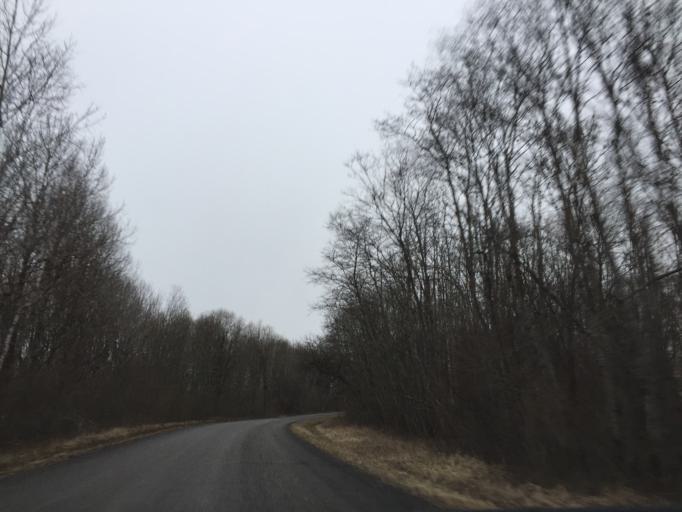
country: EE
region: Laeaene
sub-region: Lihula vald
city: Lihula
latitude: 58.6331
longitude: 23.6307
